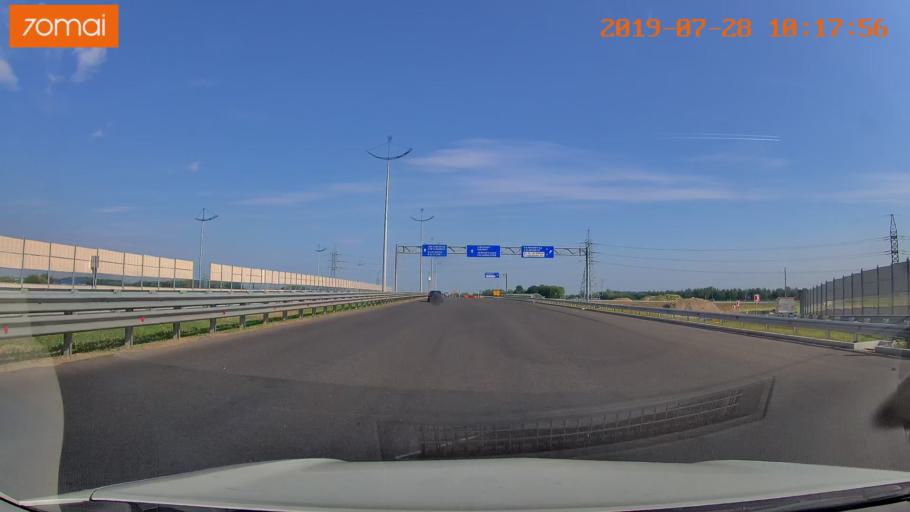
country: RU
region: Kaliningrad
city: Maloye Isakovo
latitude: 54.7459
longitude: 20.5917
